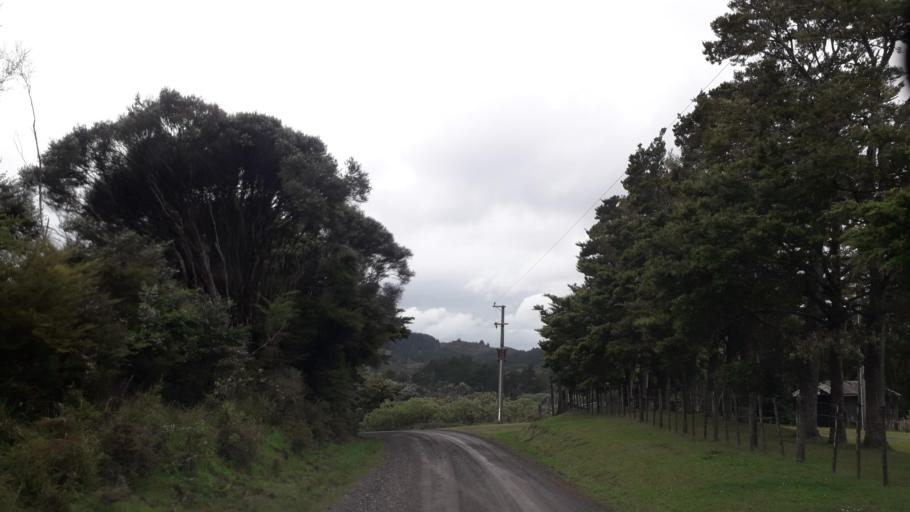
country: NZ
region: Northland
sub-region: Far North District
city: Kaitaia
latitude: -35.3888
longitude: 173.4048
